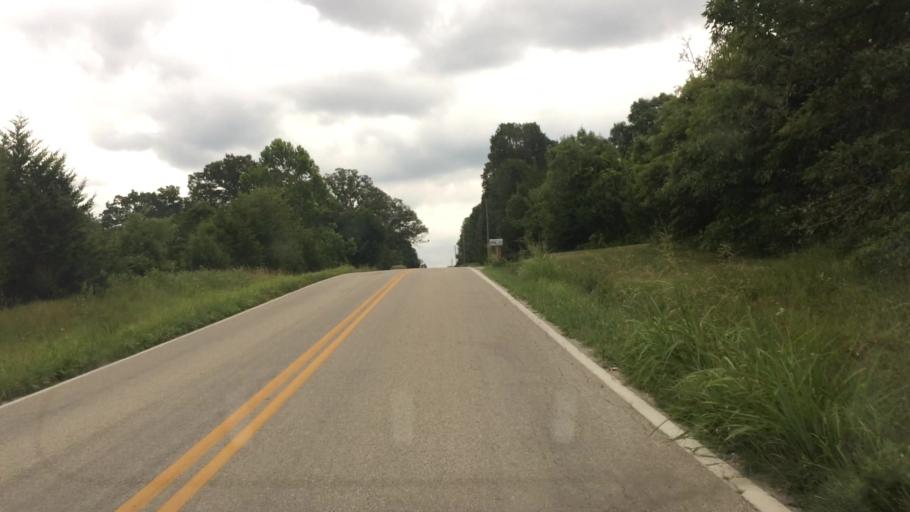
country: US
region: Missouri
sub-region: Greene County
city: Strafford
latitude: 37.3000
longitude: -93.1368
